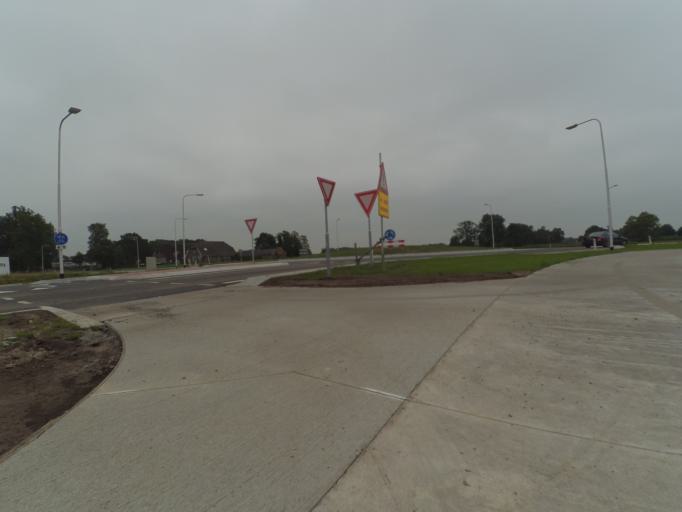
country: NL
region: Gelderland
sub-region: Gemeente Barneveld
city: Voorthuizen
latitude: 52.1504
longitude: 5.6259
